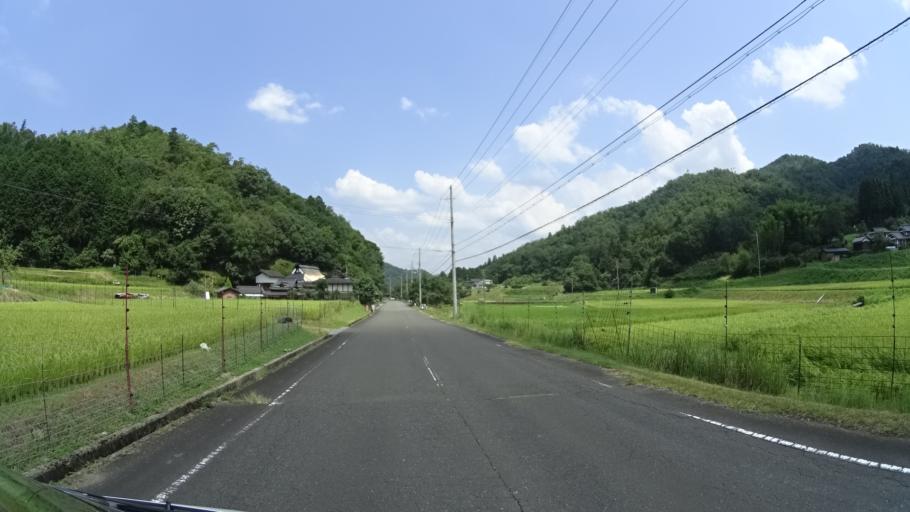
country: JP
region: Kyoto
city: Ayabe
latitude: 35.2043
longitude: 135.1969
